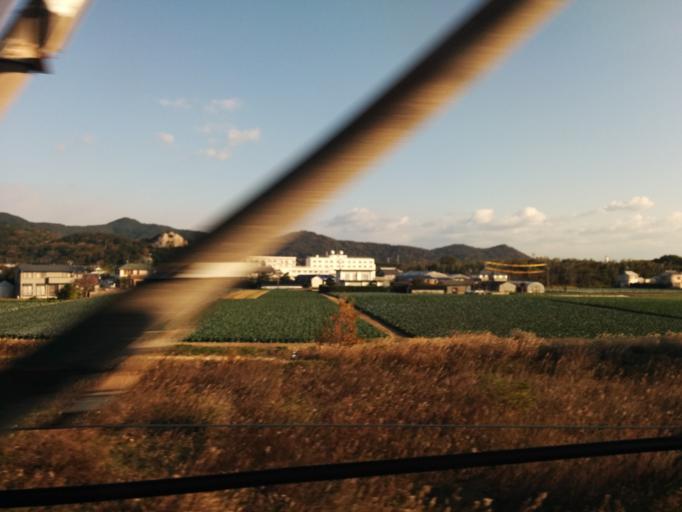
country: JP
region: Shizuoka
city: Kosai-shi
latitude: 34.7186
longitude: 137.4686
